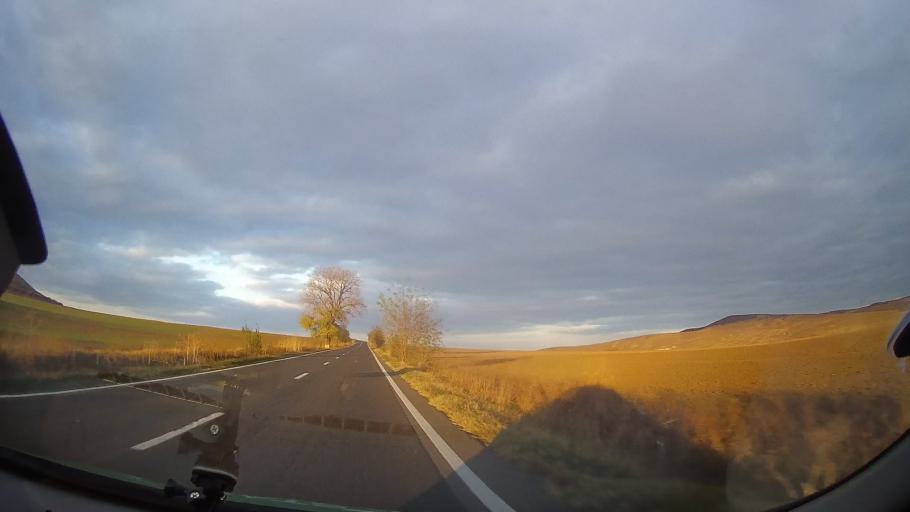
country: RO
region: Tulcea
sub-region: Comuna Nalbant
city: Nicolae Balcescu
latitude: 44.9767
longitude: 28.5454
